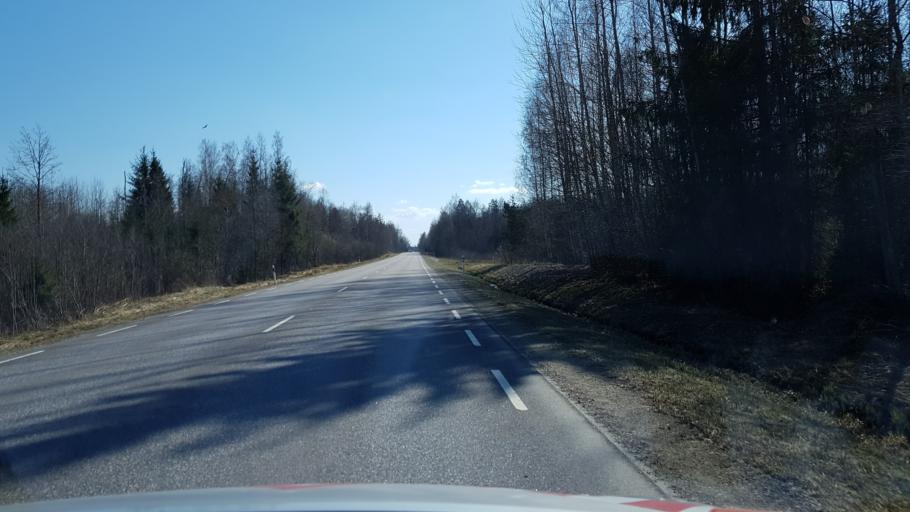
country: EE
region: Jogevamaa
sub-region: Tabivere vald
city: Tabivere
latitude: 58.6523
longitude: 26.7947
